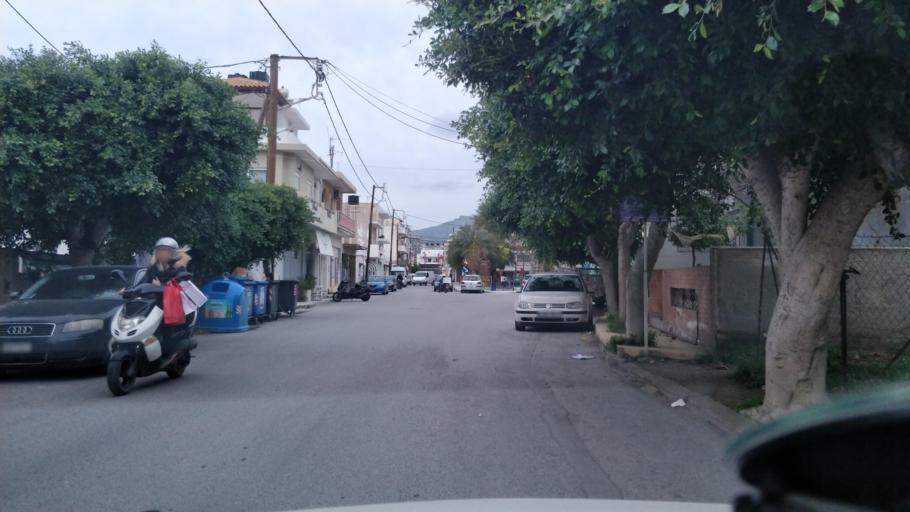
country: GR
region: Crete
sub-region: Nomos Lasithiou
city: Ierapetra
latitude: 35.0062
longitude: 25.7351
